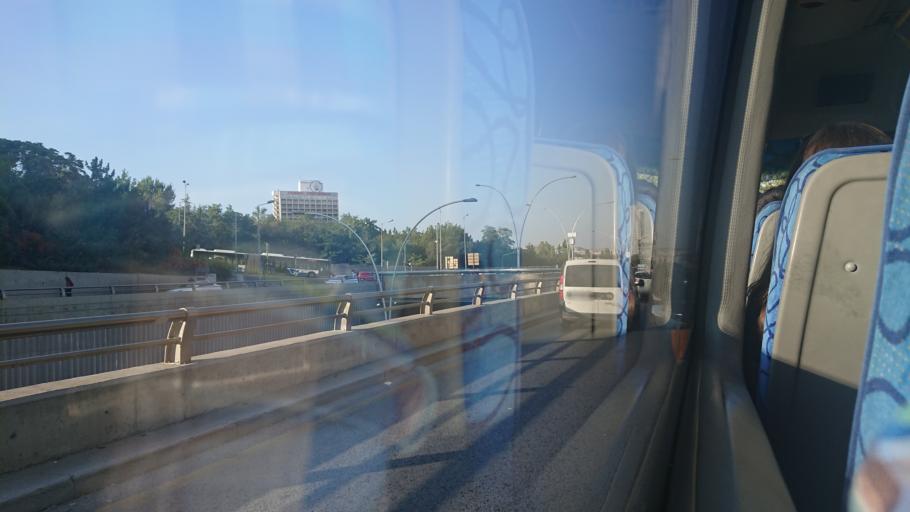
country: TR
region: Ankara
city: Ankara
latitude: 39.9305
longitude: 32.8188
